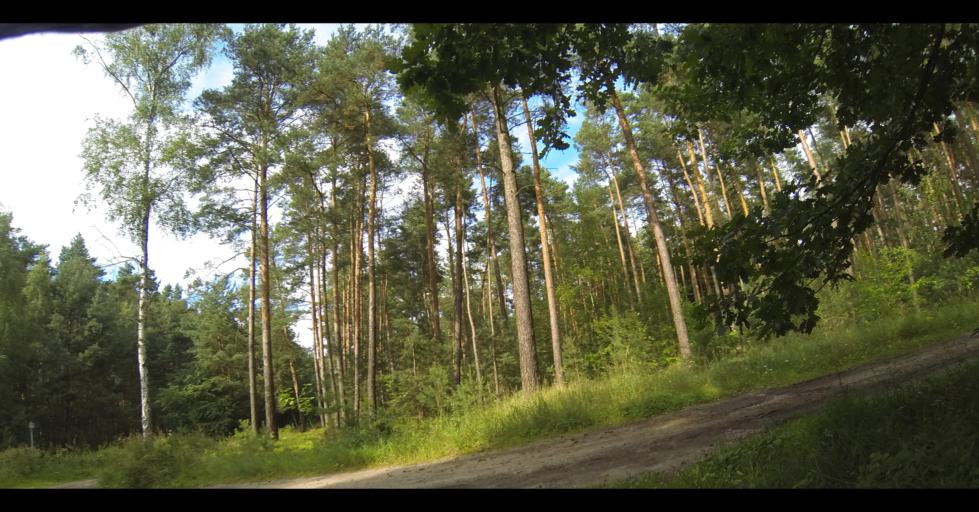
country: DE
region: Saxony
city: Radeburg
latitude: 51.2557
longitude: 13.7175
